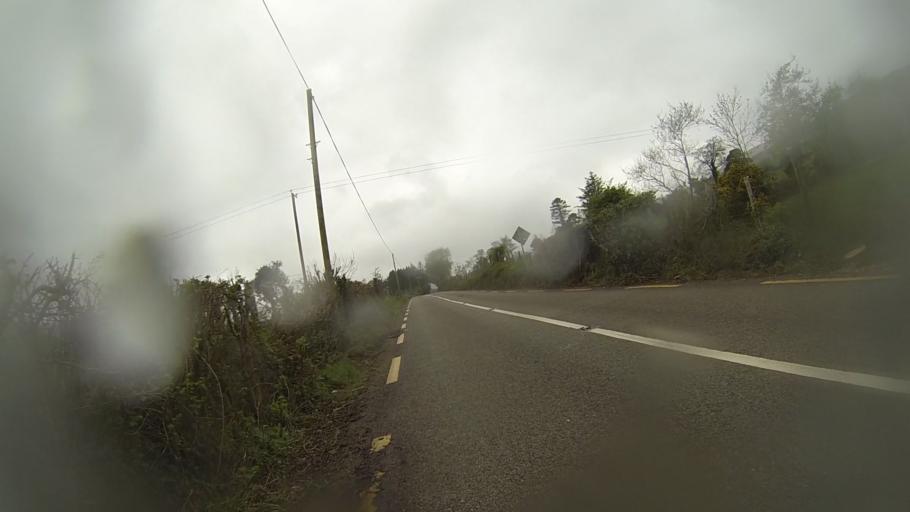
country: IE
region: Munster
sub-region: Ciarrai
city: Kenmare
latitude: 51.8151
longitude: -9.5396
